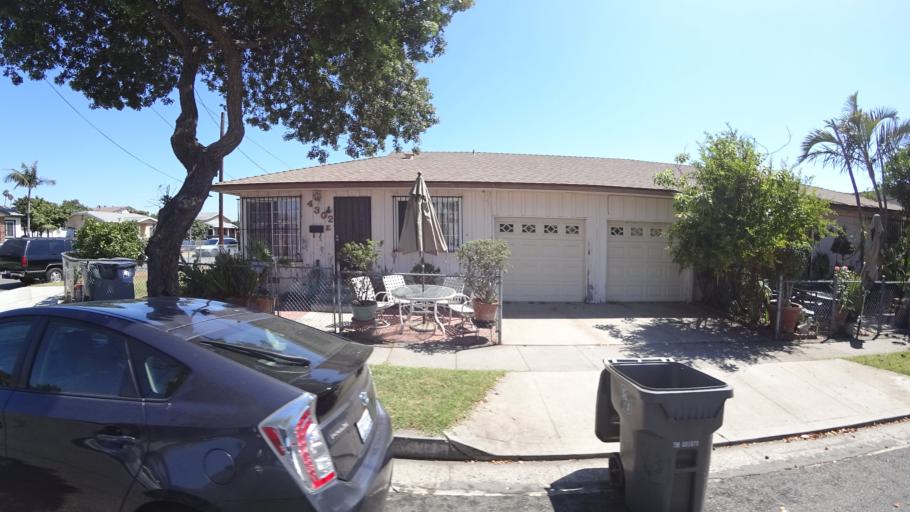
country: US
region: California
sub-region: Los Angeles County
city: Lennox
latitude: 33.9427
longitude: -118.3507
